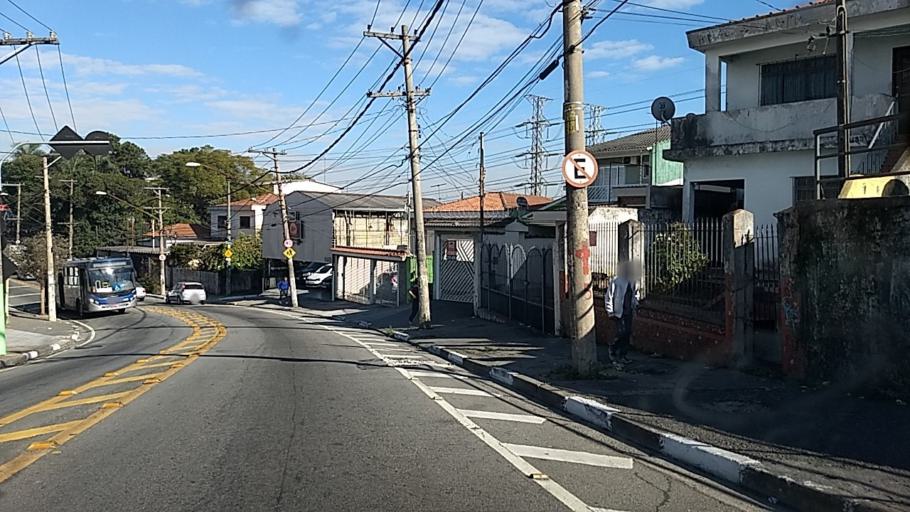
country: BR
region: Sao Paulo
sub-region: Sao Paulo
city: Sao Paulo
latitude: -23.5000
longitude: -46.5994
